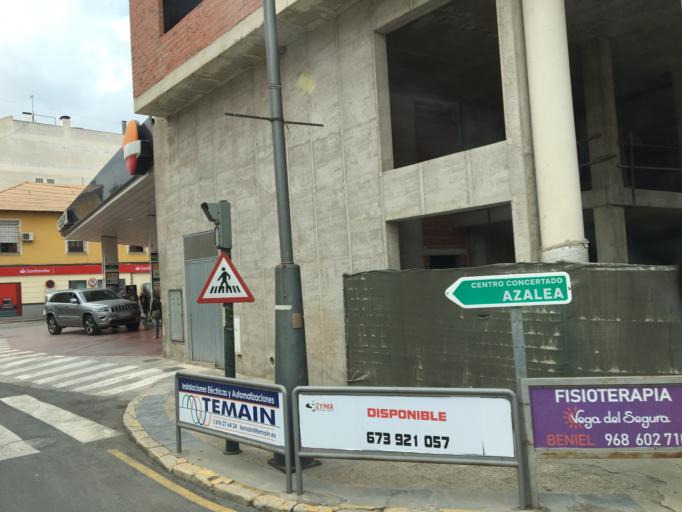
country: ES
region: Murcia
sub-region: Murcia
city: Beniel
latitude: 38.0459
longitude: -1.0018
